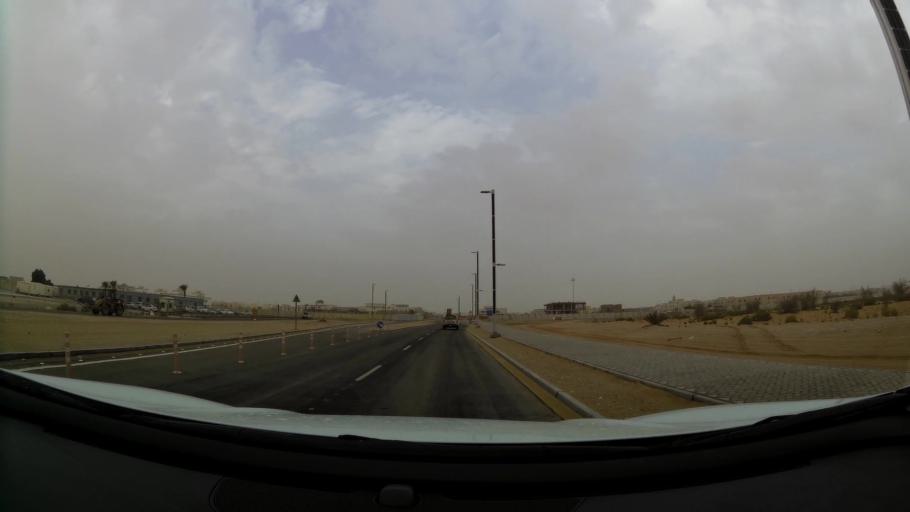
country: AE
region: Abu Dhabi
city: Abu Dhabi
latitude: 24.4181
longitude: 54.6112
